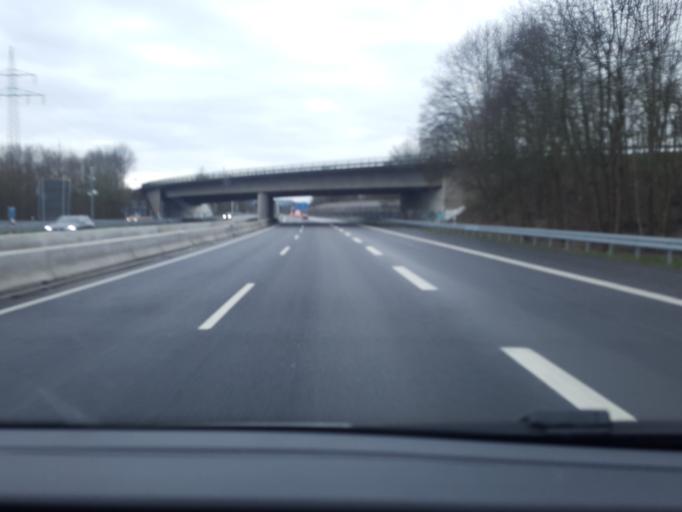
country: DE
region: North Rhine-Westphalia
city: Bad Oeynhausen
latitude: 52.2181
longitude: 8.8258
